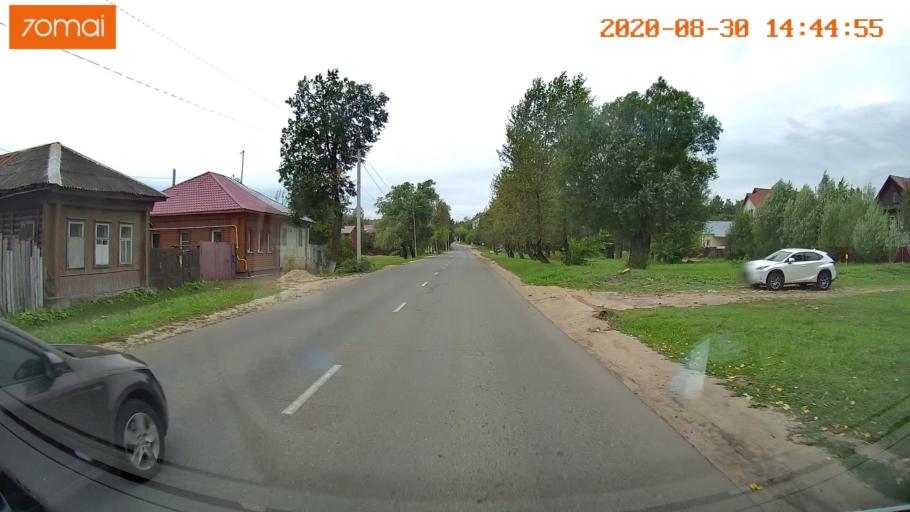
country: RU
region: Ivanovo
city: Kineshma
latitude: 57.4420
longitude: 42.1592
